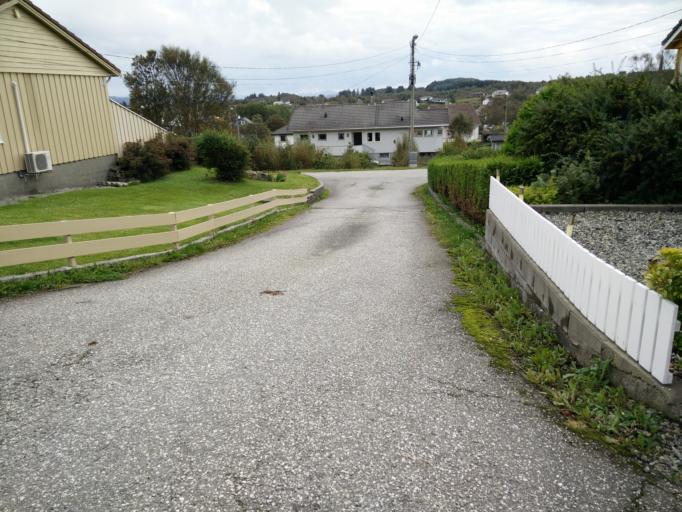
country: NO
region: Hordaland
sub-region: Sveio
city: Sveio
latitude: 59.6063
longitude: 5.2104
